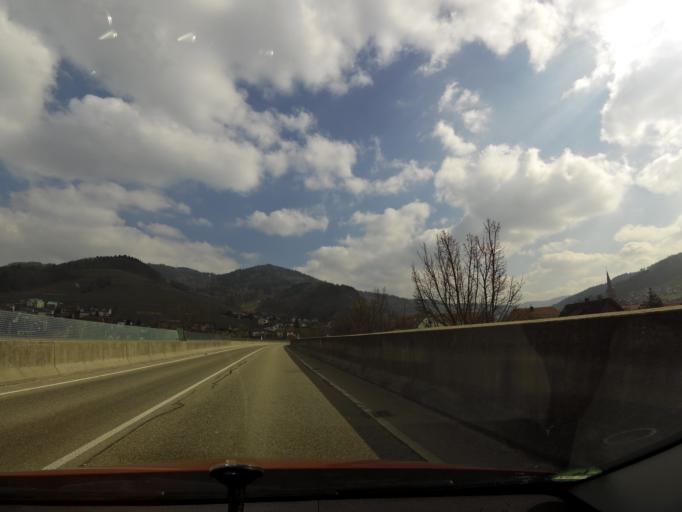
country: DE
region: Baden-Wuerttemberg
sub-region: Freiburg Region
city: Kappelrodeck
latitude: 48.5938
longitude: 8.1148
